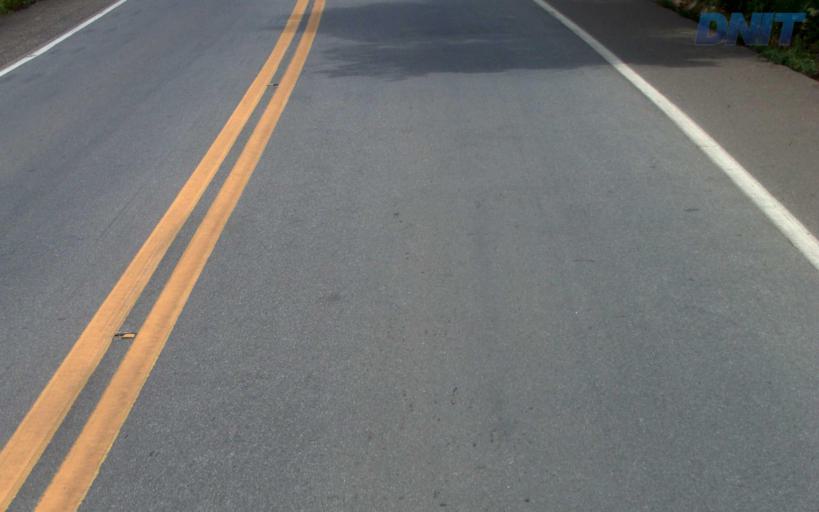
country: BR
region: Minas Gerais
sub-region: Belo Oriente
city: Belo Oriente
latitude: -19.1348
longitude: -42.2132
